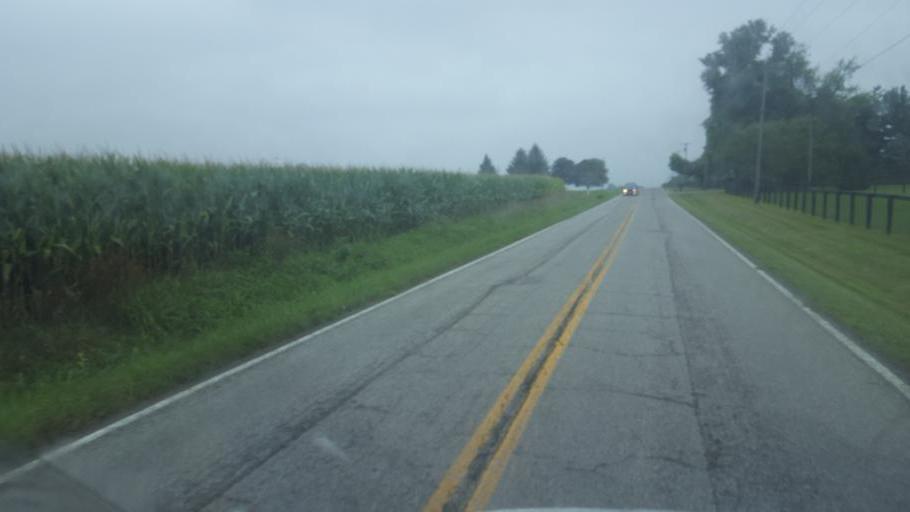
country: US
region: Ohio
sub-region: Knox County
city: Centerburg
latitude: 40.2674
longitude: -82.6915
